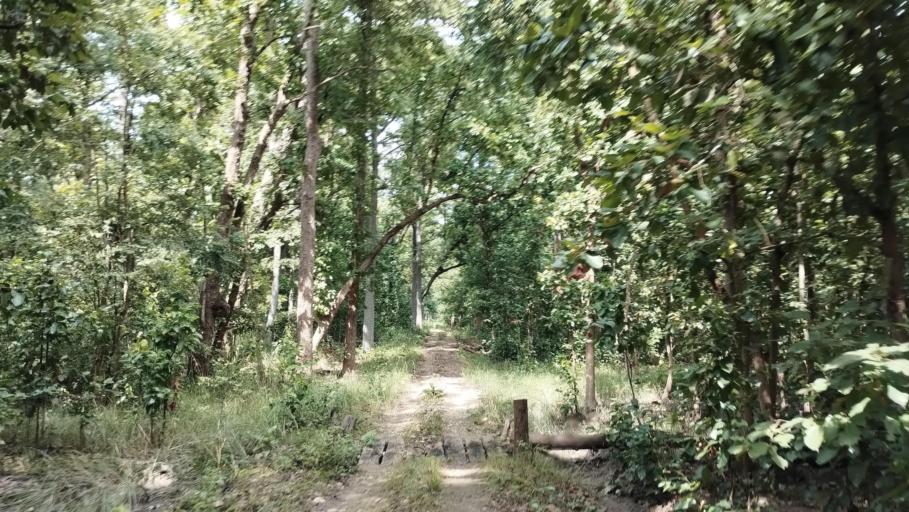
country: NP
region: Far Western
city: Tikapur
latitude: 28.5113
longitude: 81.2700
